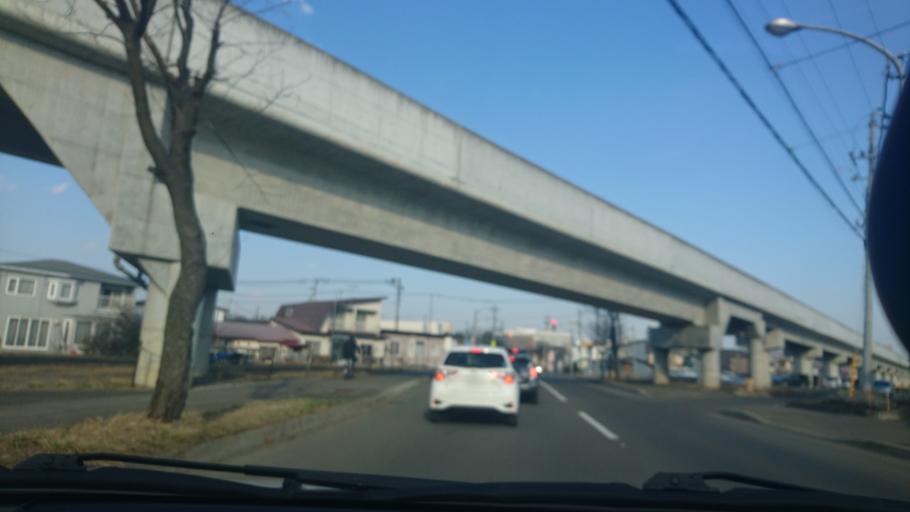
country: JP
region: Hokkaido
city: Obihiro
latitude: 42.9250
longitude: 143.1874
